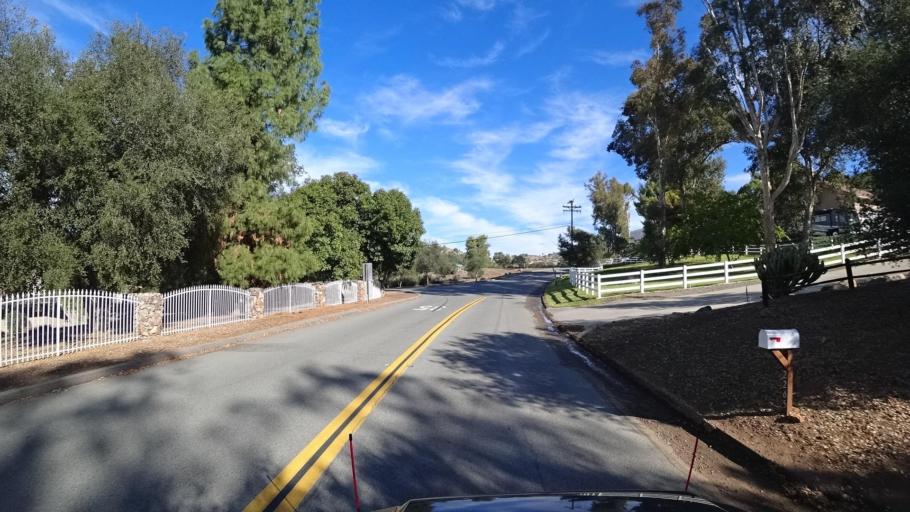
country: US
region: California
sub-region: San Diego County
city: Alpine
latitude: 32.8202
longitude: -116.7487
